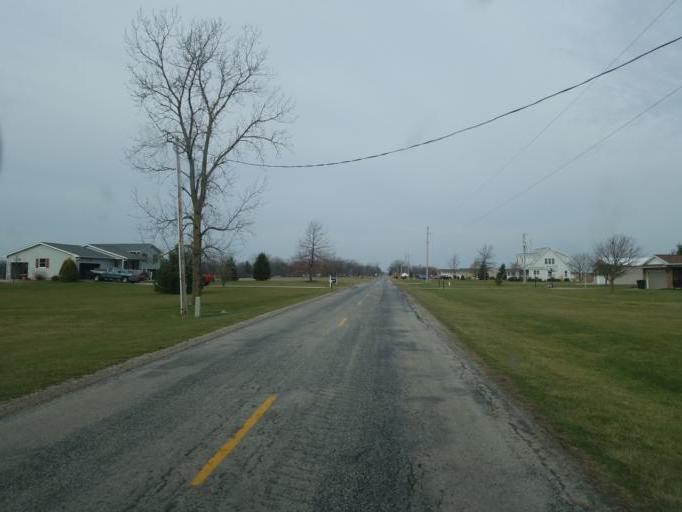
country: US
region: Ohio
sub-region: Marion County
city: Marion
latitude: 40.6521
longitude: -83.0686
